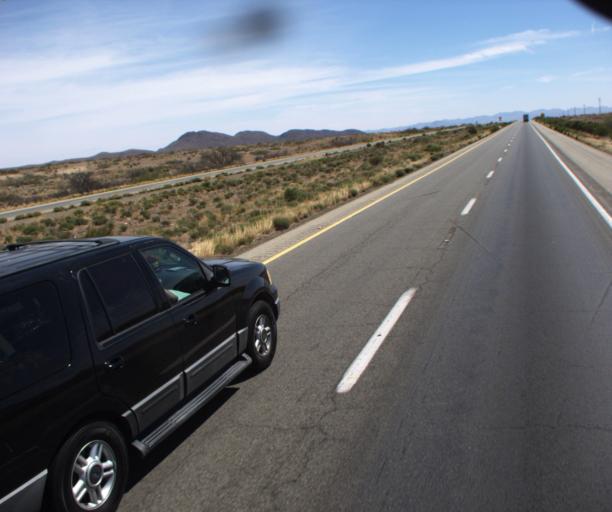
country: US
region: Arizona
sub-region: Cochise County
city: Willcox
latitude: 32.3624
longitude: -109.6416
